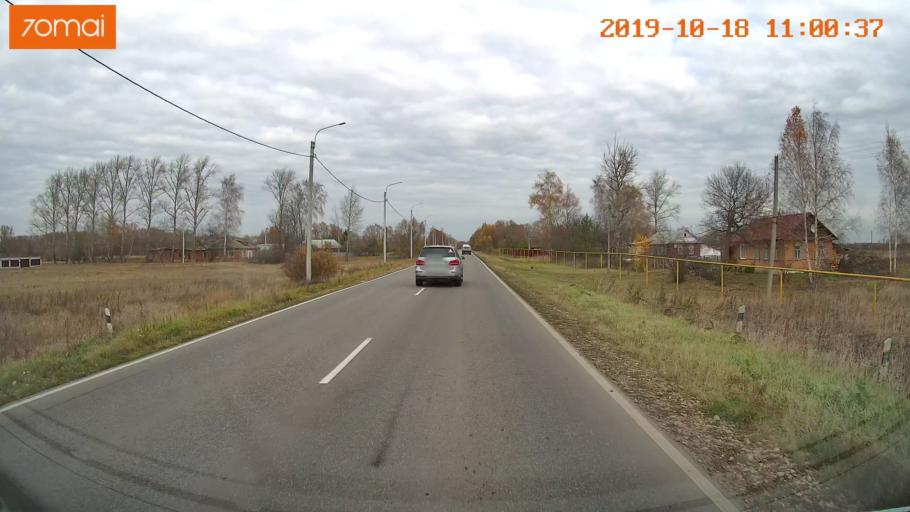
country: RU
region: Tula
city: Yepifan'
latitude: 53.8453
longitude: 38.5527
